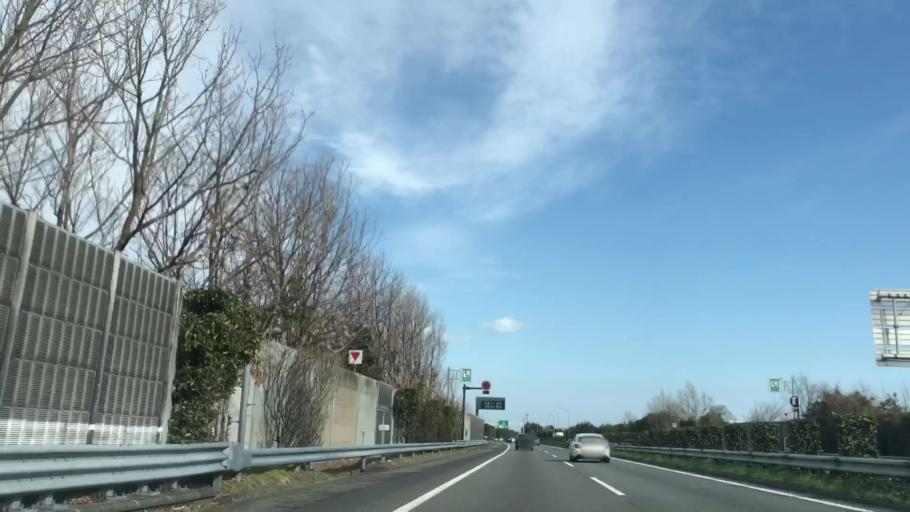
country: JP
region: Shizuoka
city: Hamakita
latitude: 34.7481
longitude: 137.7805
